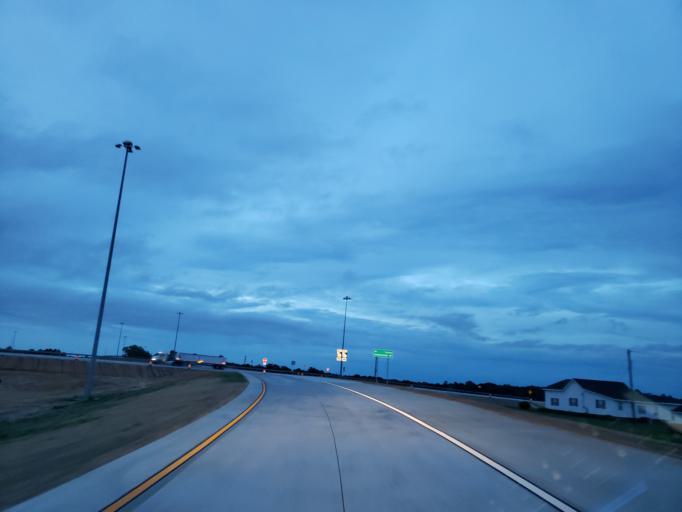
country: US
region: Georgia
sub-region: Dooly County
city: Vienna
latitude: 32.1224
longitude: -83.7594
